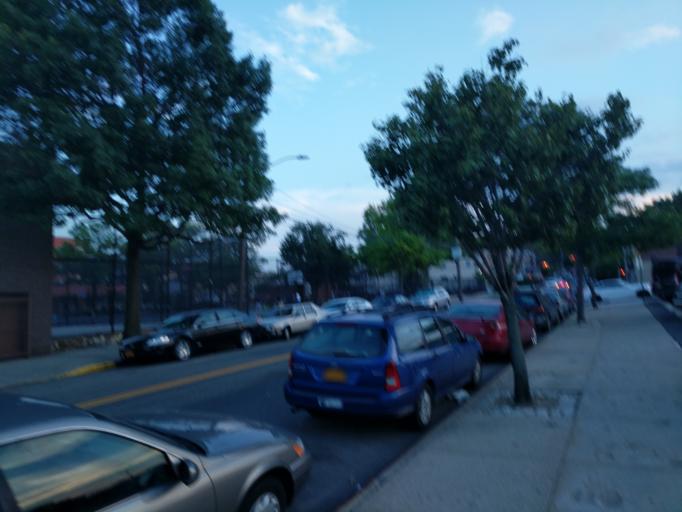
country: US
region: New York
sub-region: Queens County
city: Long Island City
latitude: 40.7782
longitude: -73.9025
